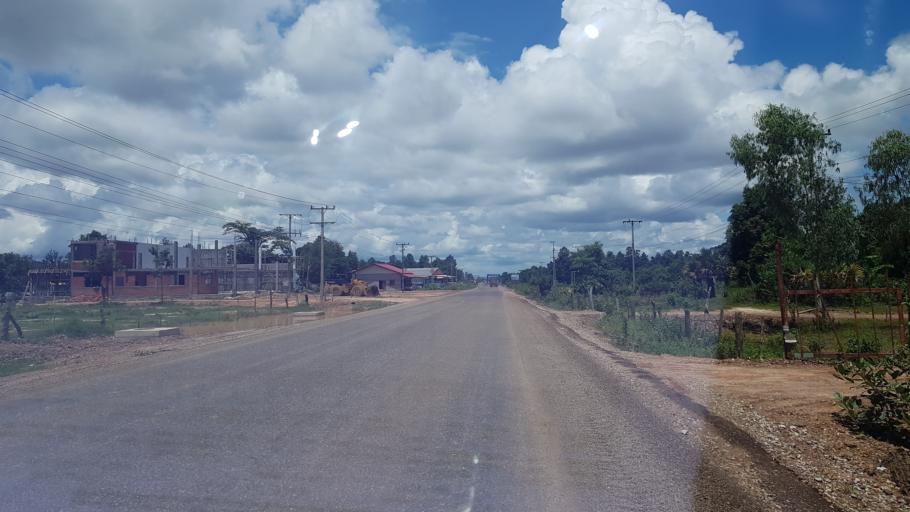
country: LA
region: Vientiane
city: Vientiane
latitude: 18.1047
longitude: 102.5654
